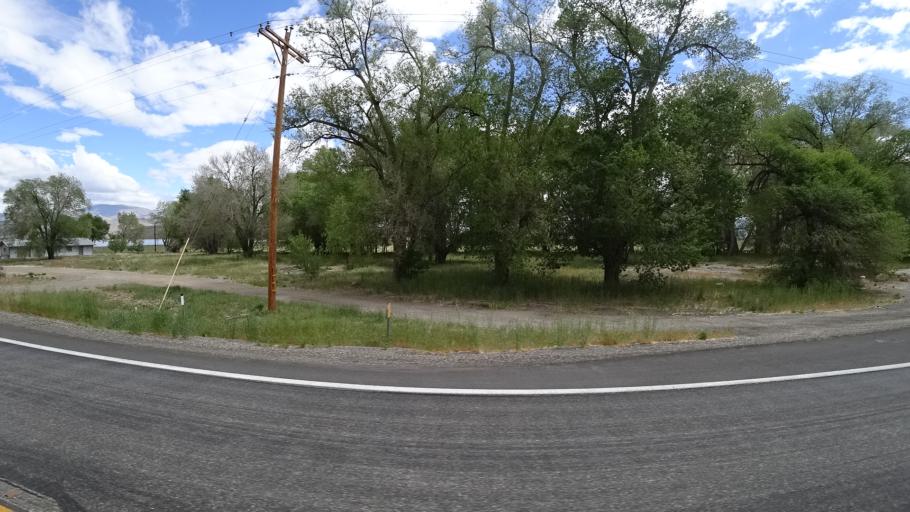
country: US
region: Nevada
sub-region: Lyon County
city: Smith Valley
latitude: 38.6507
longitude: -119.5339
